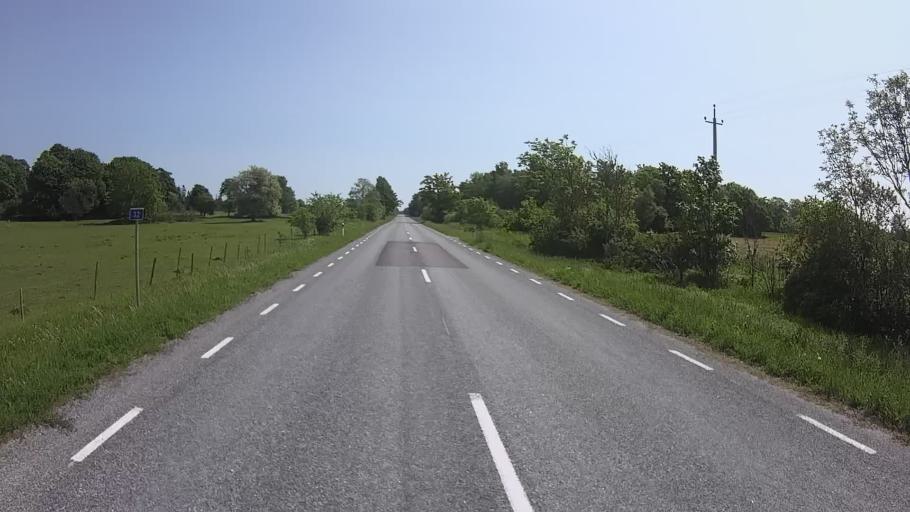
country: EE
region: Saare
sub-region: Kuressaare linn
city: Kuressaare
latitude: 58.3684
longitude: 22.0497
